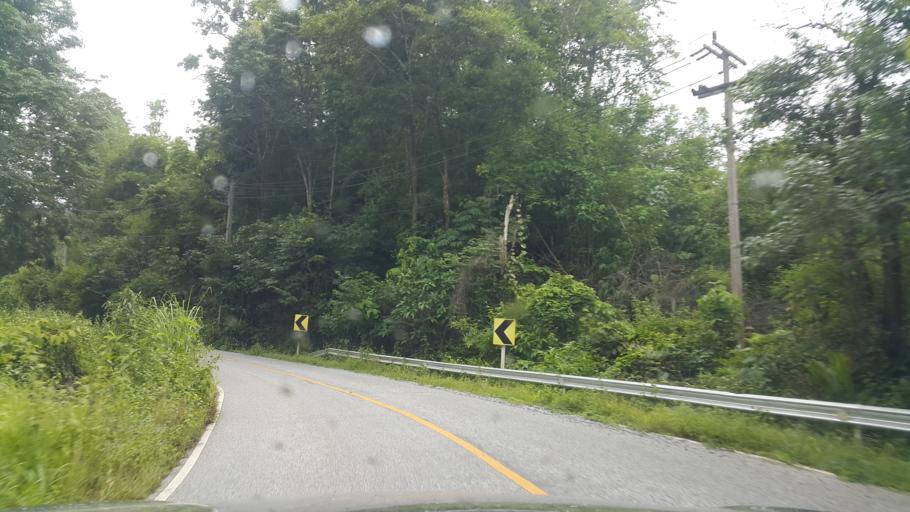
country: TH
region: Loei
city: Na Haeo
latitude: 17.5053
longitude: 100.8163
